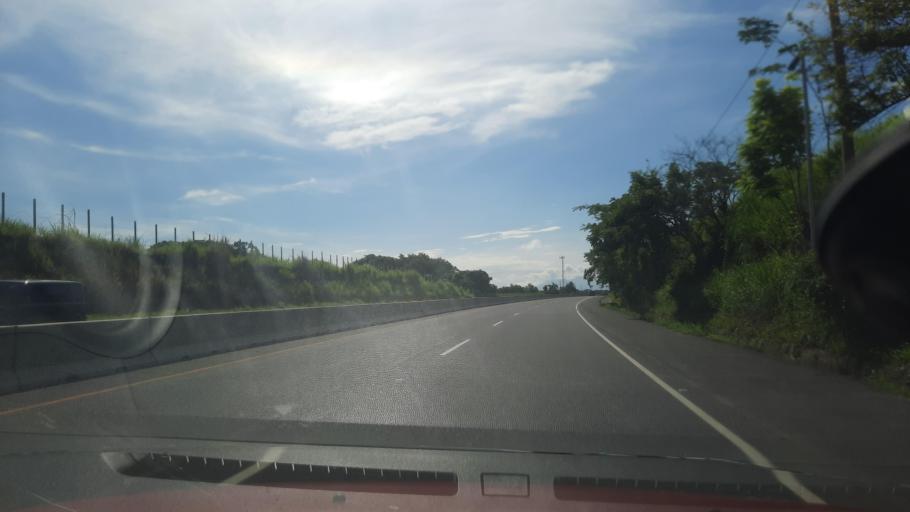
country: SV
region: La Paz
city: Santiago Nonualco
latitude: 13.4872
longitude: -88.9658
